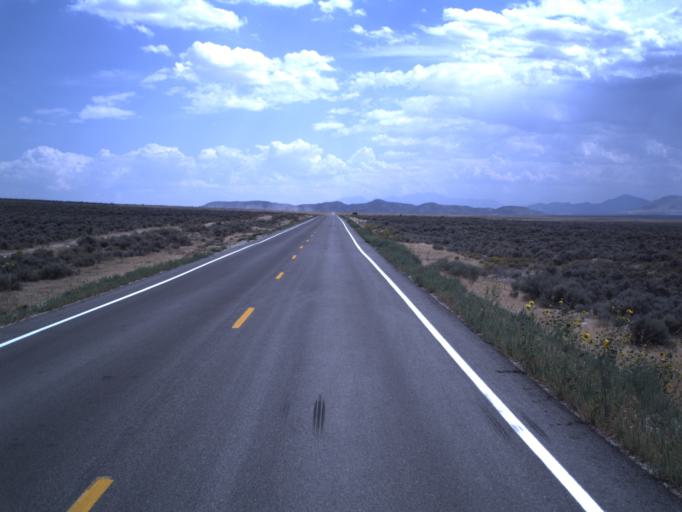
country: US
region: Utah
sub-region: Tooele County
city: Tooele
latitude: 40.2845
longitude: -112.2628
